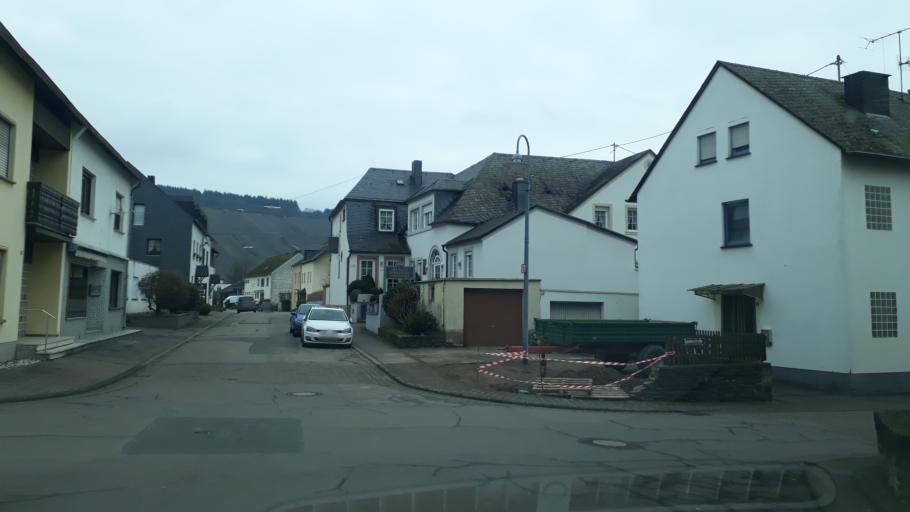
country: DE
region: Rheinland-Pfalz
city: Mehring
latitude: 49.7967
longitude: 6.8253
